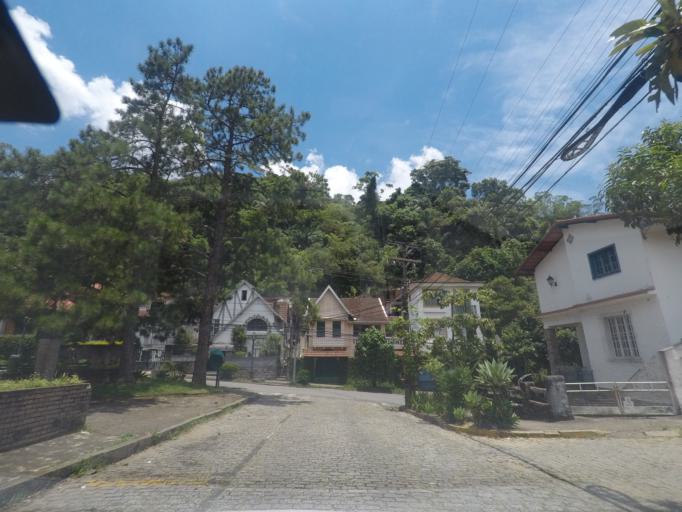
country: BR
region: Rio de Janeiro
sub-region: Petropolis
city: Petropolis
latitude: -22.5053
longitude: -43.1722
